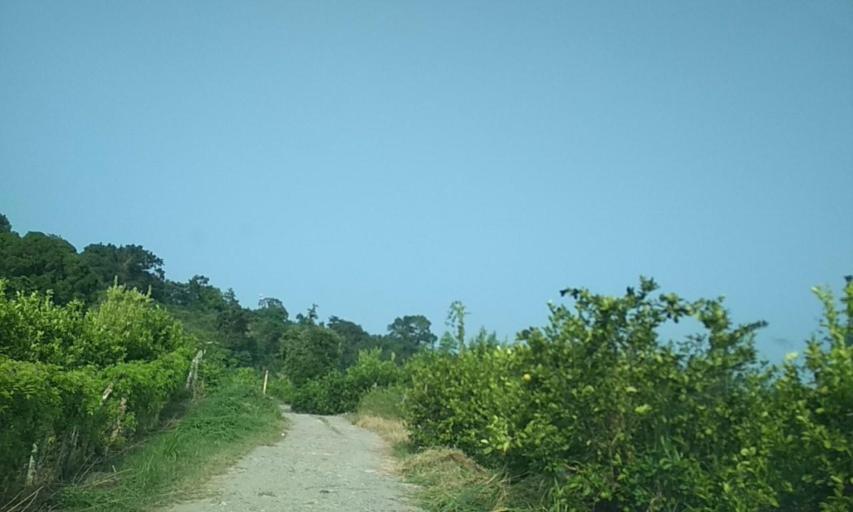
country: MX
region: Veracruz
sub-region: Misantla
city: La Defensa
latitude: 20.0502
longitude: -96.9811
